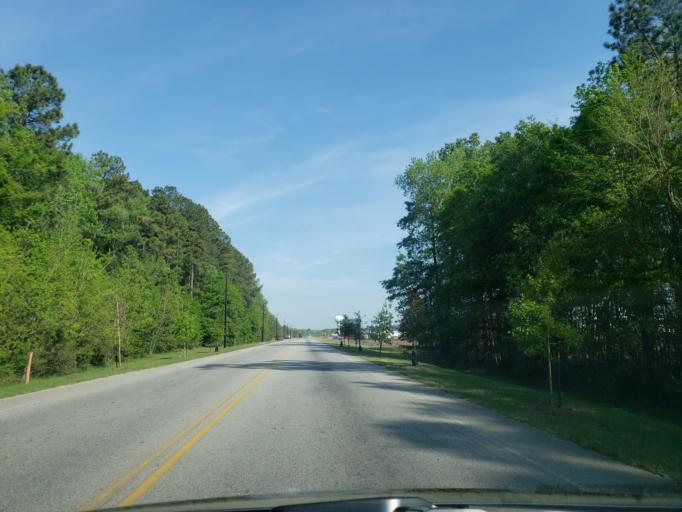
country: US
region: Georgia
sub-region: Chatham County
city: Garden City
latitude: 32.1036
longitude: -81.1925
